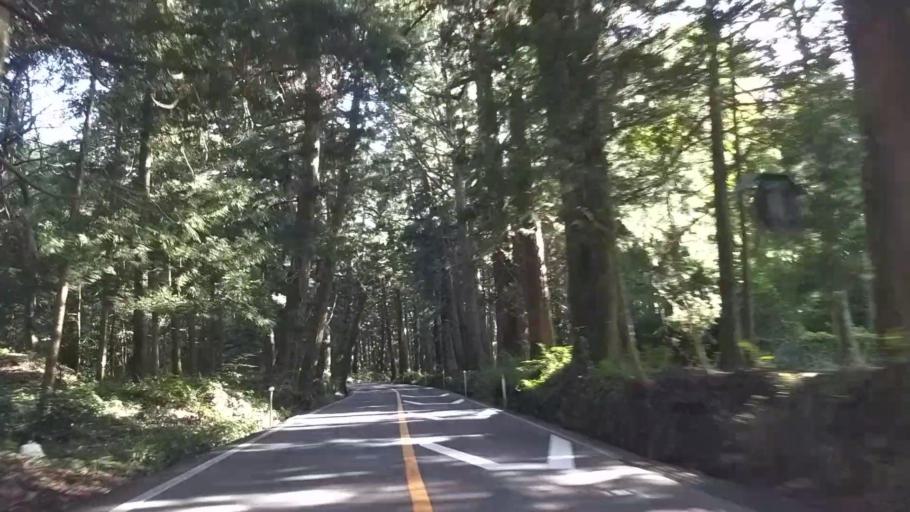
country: JP
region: Tochigi
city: Imaichi
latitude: 36.7588
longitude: 139.7095
